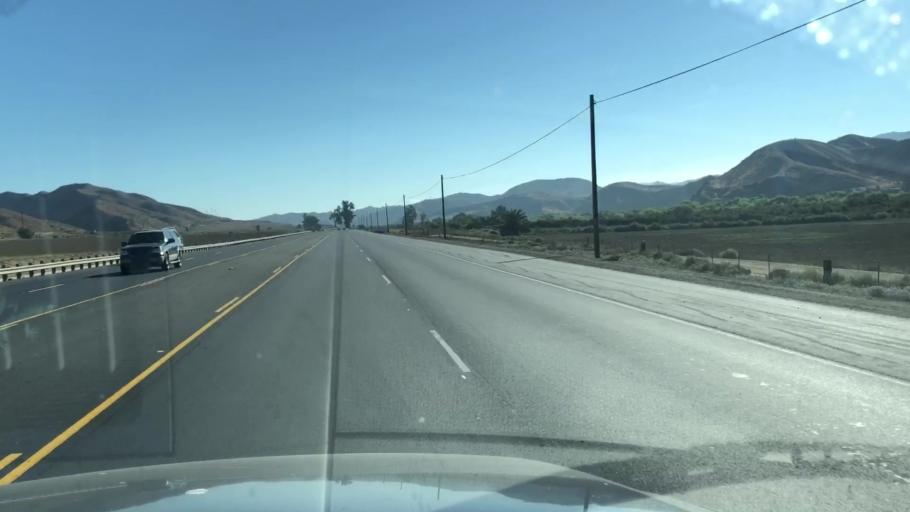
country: US
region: California
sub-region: Los Angeles County
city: Val Verde
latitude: 34.4050
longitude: -118.6990
